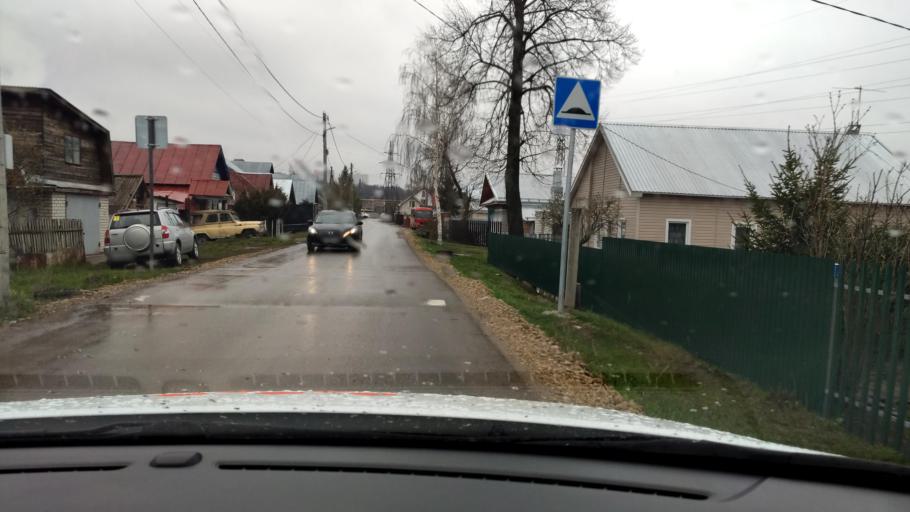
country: RU
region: Tatarstan
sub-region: Gorod Kazan'
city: Kazan
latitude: 55.7249
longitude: 49.1472
